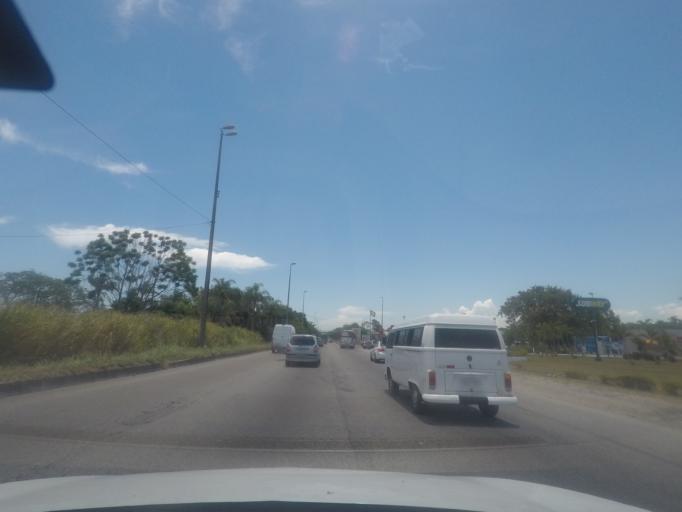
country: BR
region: Rio de Janeiro
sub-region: Itaguai
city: Itaguai
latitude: -22.8924
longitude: -43.6717
